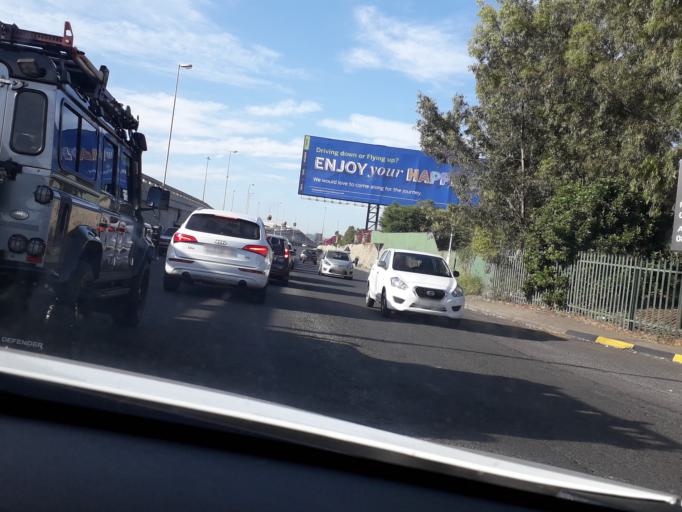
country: ZA
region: Gauteng
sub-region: City of Johannesburg Metropolitan Municipality
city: Modderfontein
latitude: -26.1646
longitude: 28.1329
